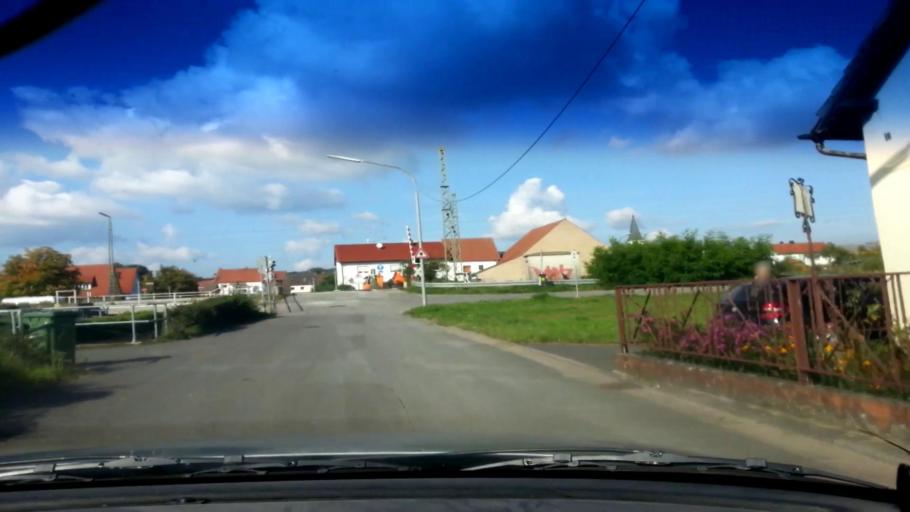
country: DE
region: Bavaria
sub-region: Upper Franconia
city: Oberhaid
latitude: 49.9292
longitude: 10.8146
